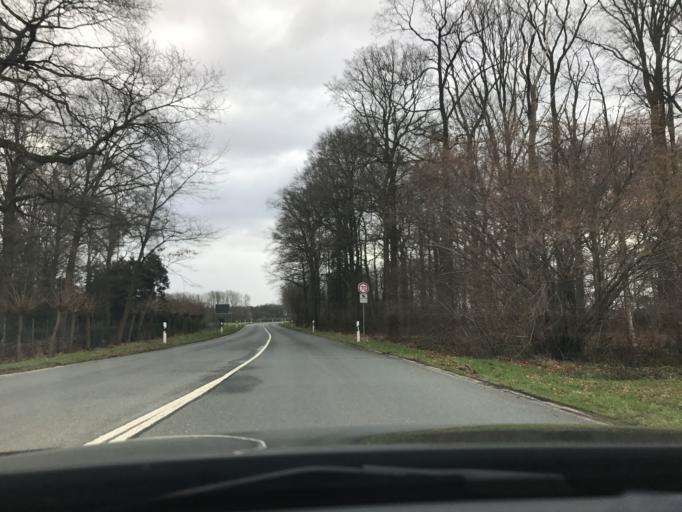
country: DE
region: North Rhine-Westphalia
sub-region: Regierungsbezirk Dusseldorf
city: Wachtendonk
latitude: 51.4407
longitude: 6.3375
